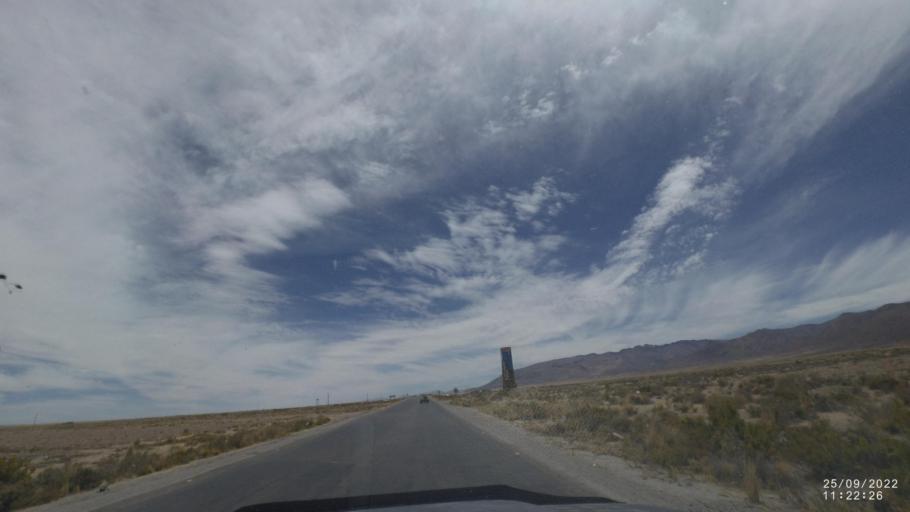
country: BO
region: Oruro
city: Challapata
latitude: -19.1257
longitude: -66.7685
